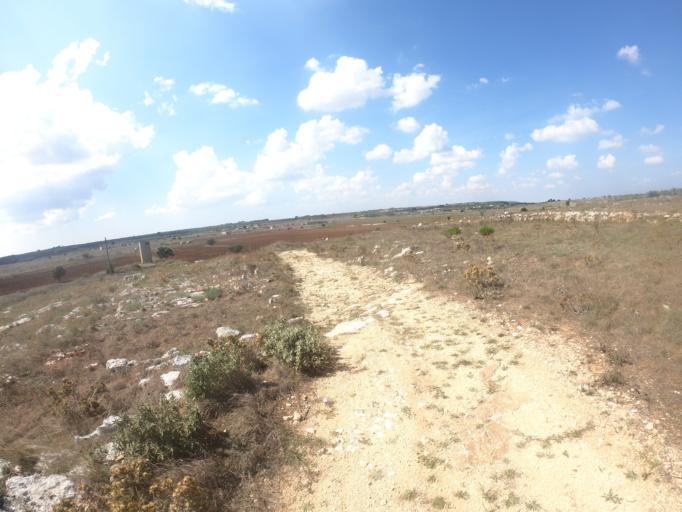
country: IT
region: Apulia
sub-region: Provincia di Lecce
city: Ruffano
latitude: 39.9501
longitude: 18.2641
